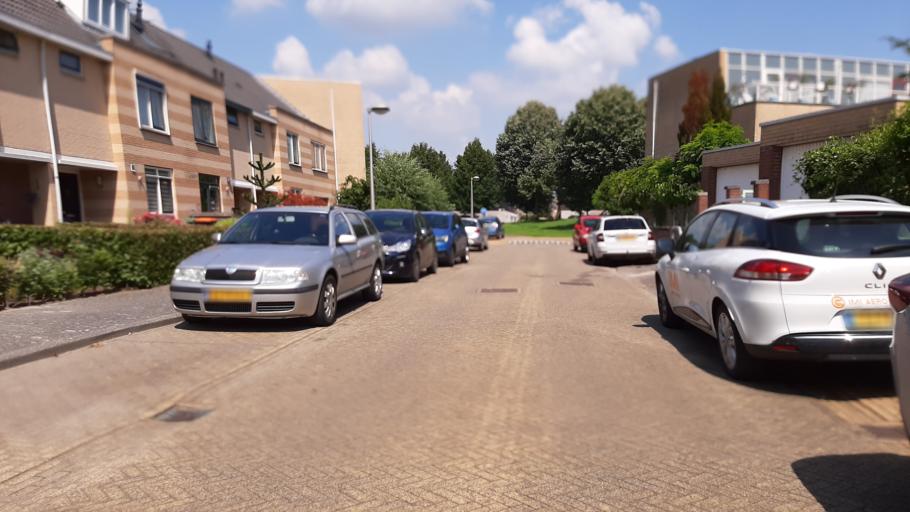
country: NL
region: Flevoland
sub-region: Gemeente Zeewolde
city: Zeewolde
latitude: 52.3318
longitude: 5.5179
